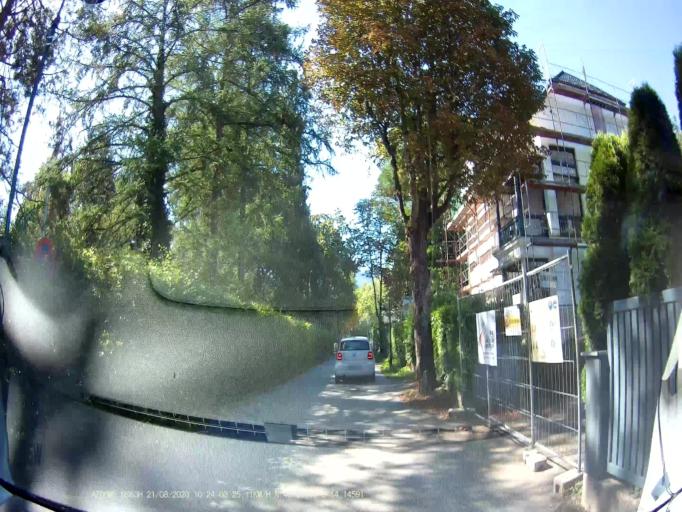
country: AT
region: Carinthia
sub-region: Politischer Bezirk Klagenfurt Land
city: Maria Worth
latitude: 46.6343
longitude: 14.1458
